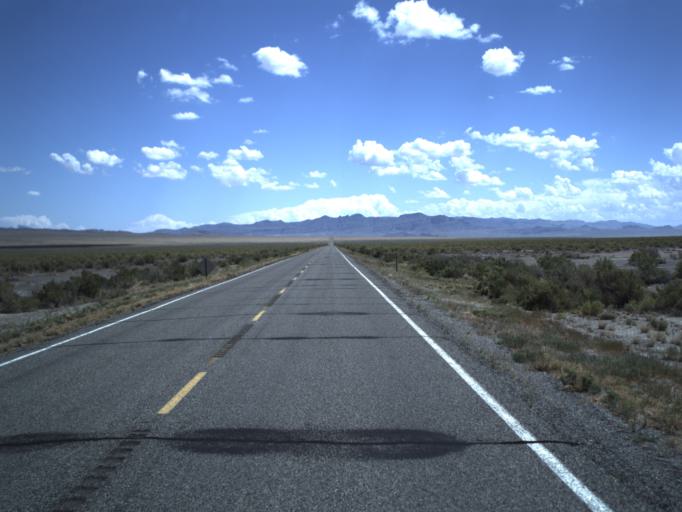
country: US
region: Nevada
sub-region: White Pine County
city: McGill
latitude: 39.0478
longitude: -113.9265
